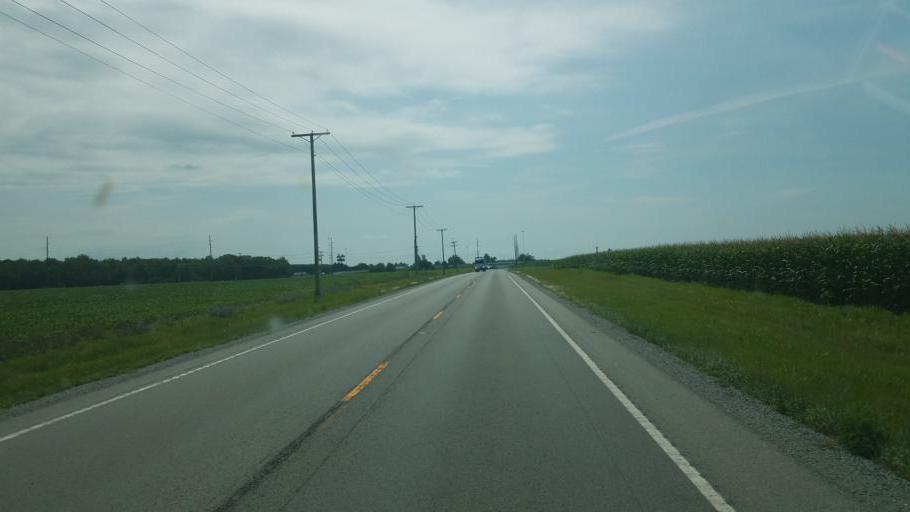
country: US
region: Ohio
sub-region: Wyandot County
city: Upper Sandusky
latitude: 40.8636
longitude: -83.3079
